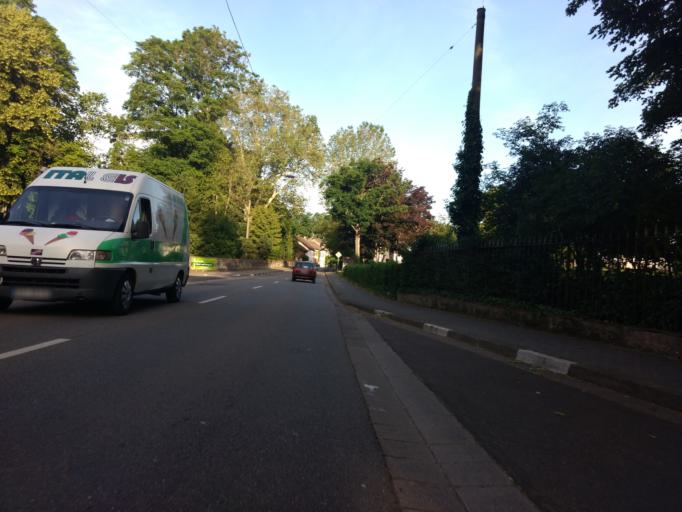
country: DE
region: Saarland
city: Wallerfangen
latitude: 49.3283
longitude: 6.7196
